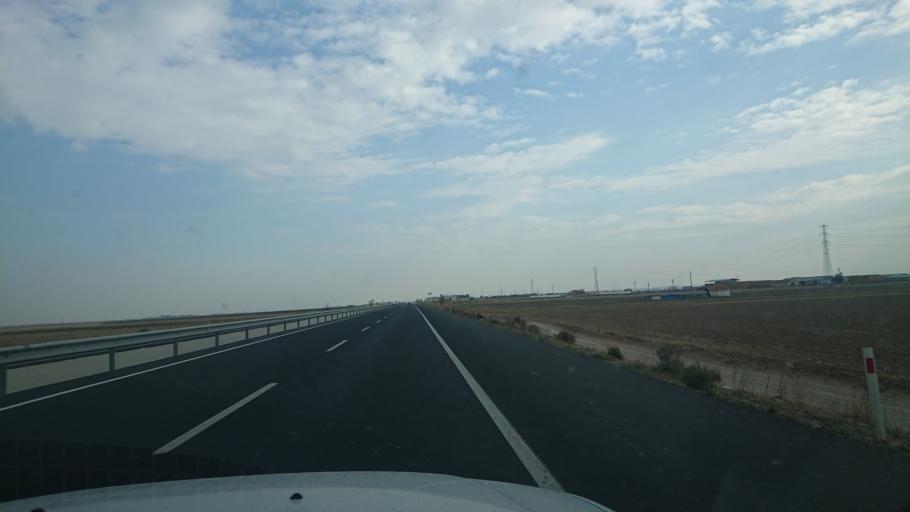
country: TR
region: Aksaray
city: Yesilova
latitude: 38.3000
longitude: 33.7952
